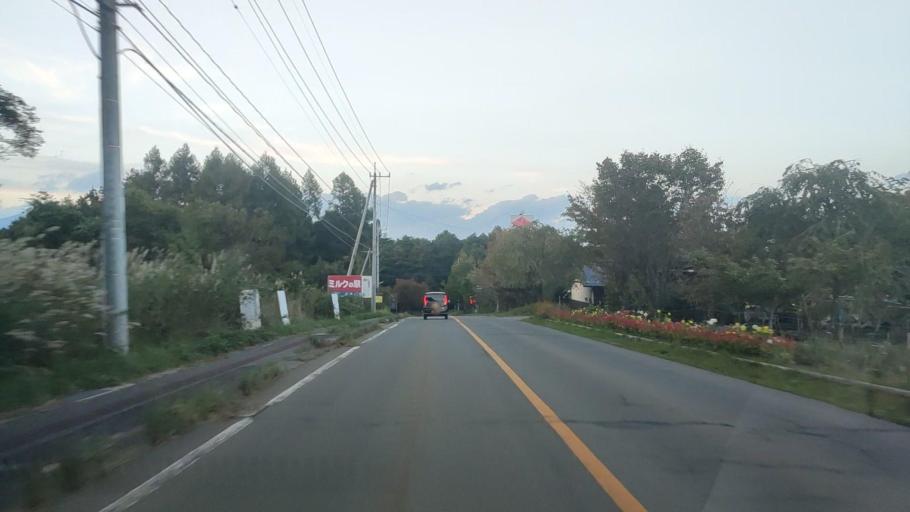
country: JP
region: Nagano
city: Komoro
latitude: 36.4766
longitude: 138.5869
